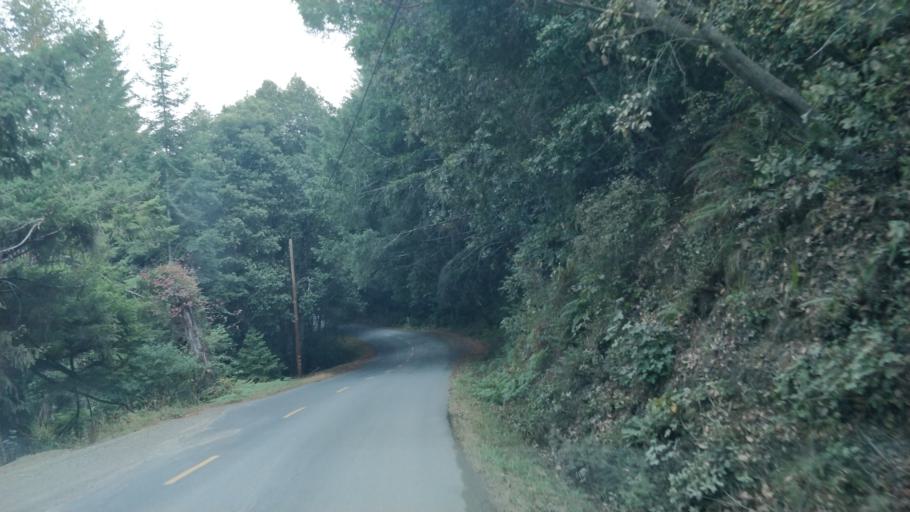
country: US
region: California
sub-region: Humboldt County
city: Rio Dell
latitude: 40.2701
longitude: -124.2056
